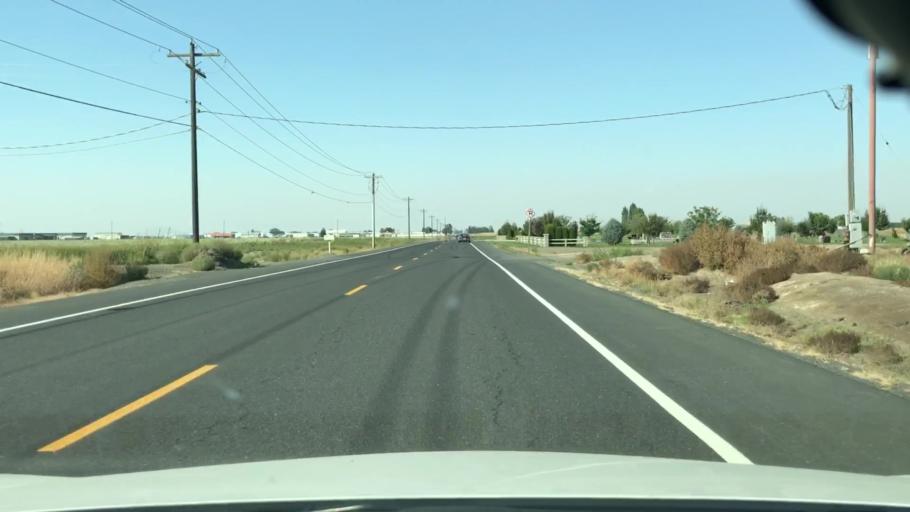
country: US
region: Washington
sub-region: Grant County
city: Moses Lake
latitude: 47.1233
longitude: -119.2358
